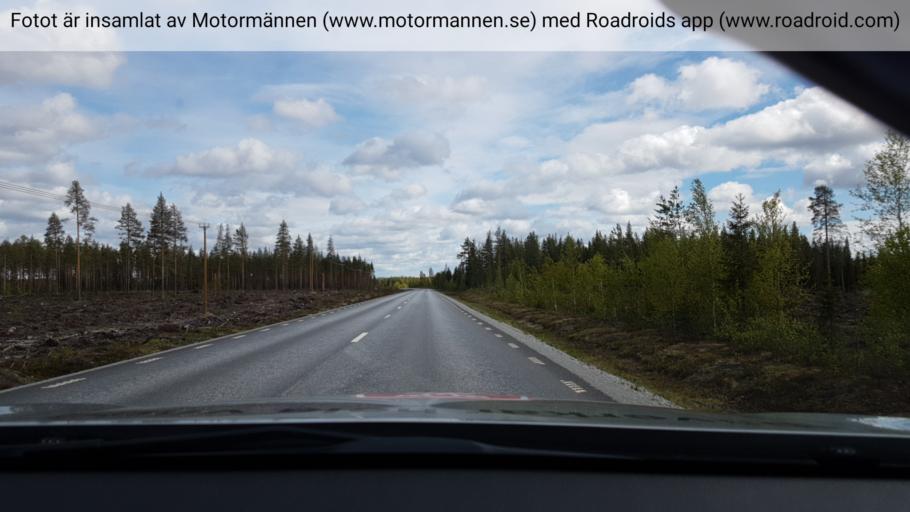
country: SE
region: Vaesterbotten
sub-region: Asele Kommun
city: Insjon
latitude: 64.1222
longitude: 18.0907
